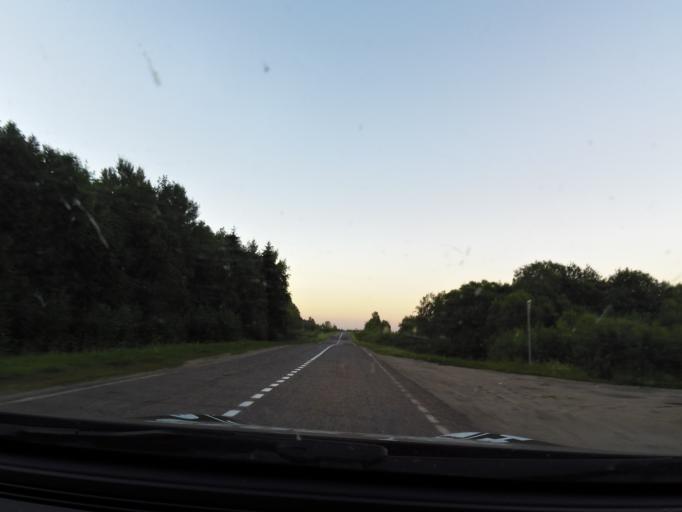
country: RU
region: Jaroslavl
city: Lyubim
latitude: 58.3356
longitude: 41.0760
